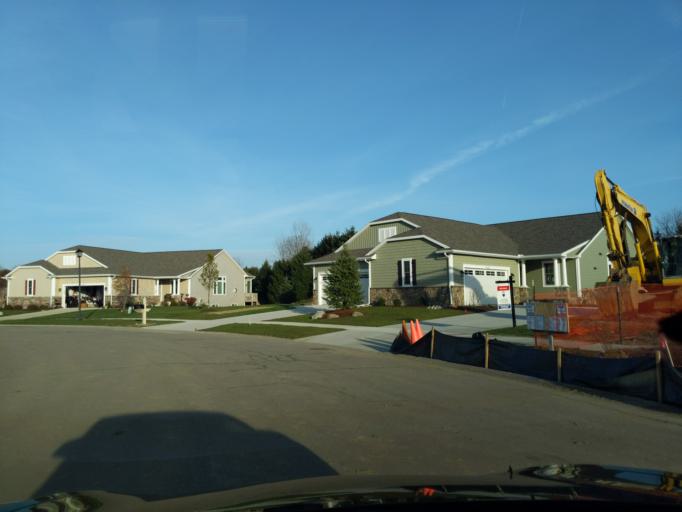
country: US
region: Michigan
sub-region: Clinton County
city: Bath
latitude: 42.7939
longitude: -84.4611
